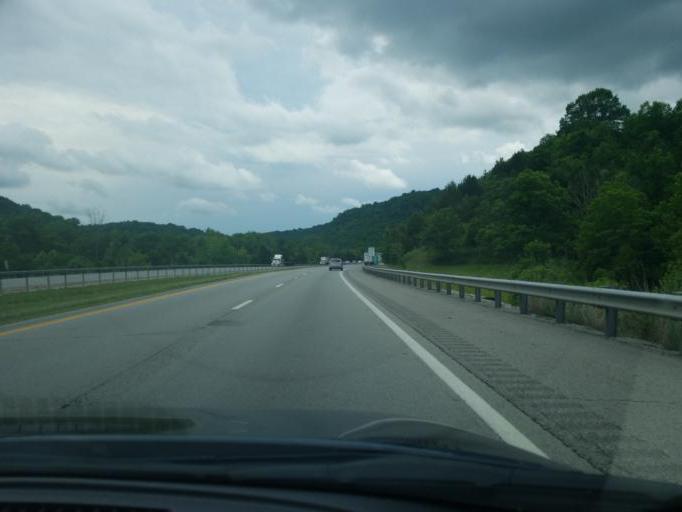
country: US
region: Kentucky
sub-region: Carroll County
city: Carrollton
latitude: 38.6142
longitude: -85.1633
